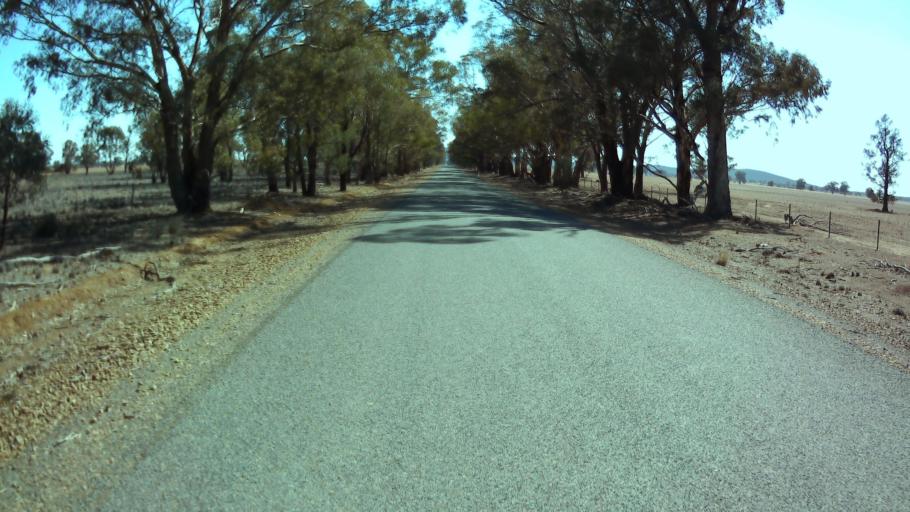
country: AU
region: New South Wales
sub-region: Weddin
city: Grenfell
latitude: -33.7231
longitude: 147.8970
